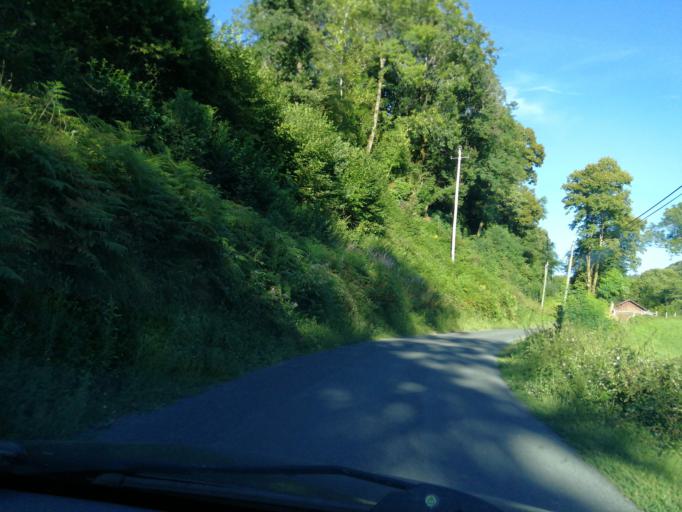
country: FR
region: Auvergne
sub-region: Departement du Cantal
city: Saint-Cernin
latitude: 45.1011
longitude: 2.5356
